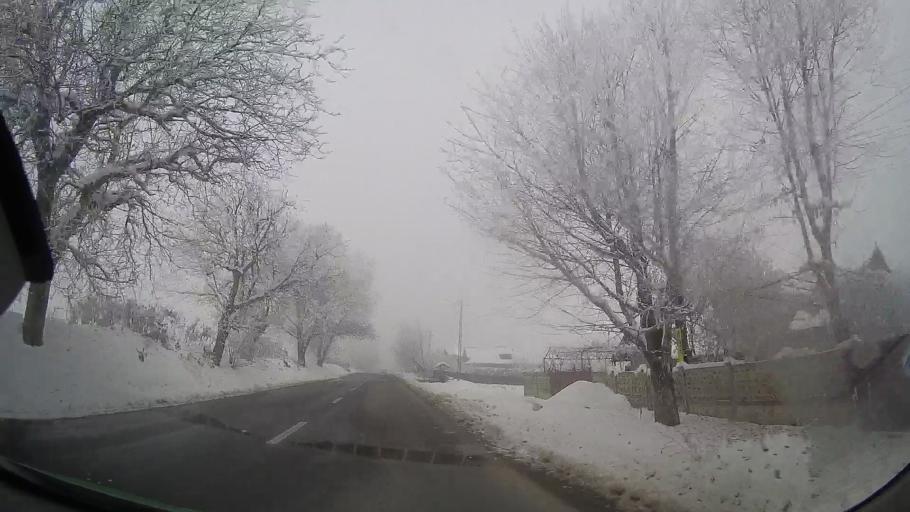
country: RO
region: Iasi
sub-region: Comuna Valea Seaca
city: Valea Seaca
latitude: 47.2919
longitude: 26.6755
